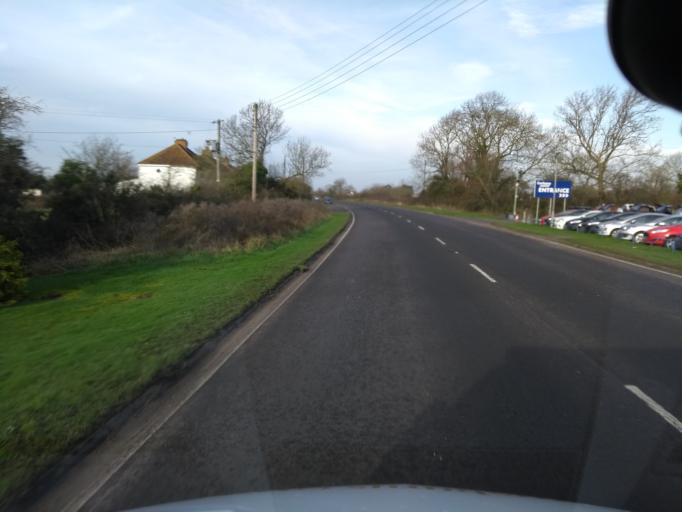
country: GB
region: England
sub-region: North Somerset
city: Bleadon
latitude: 51.2818
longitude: -2.9363
